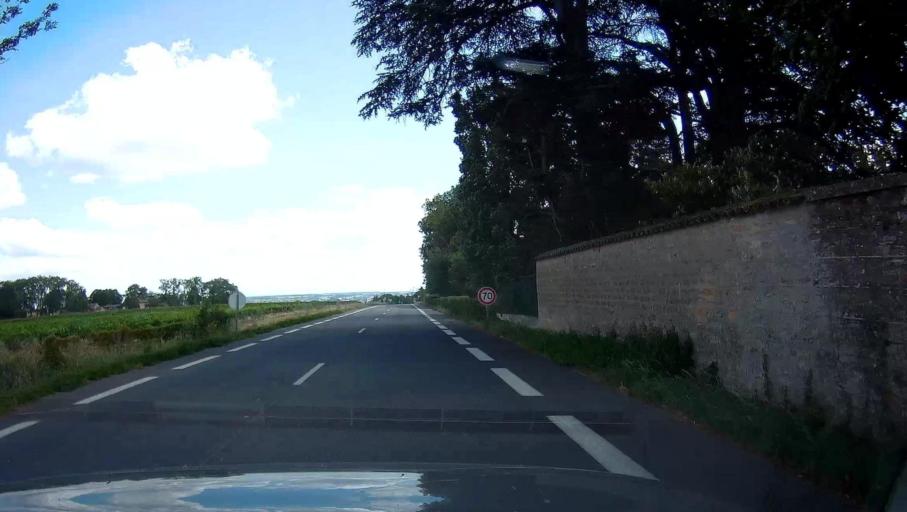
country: FR
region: Rhone-Alpes
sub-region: Departement du Rhone
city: Gleize
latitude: 45.9927
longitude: 4.6896
